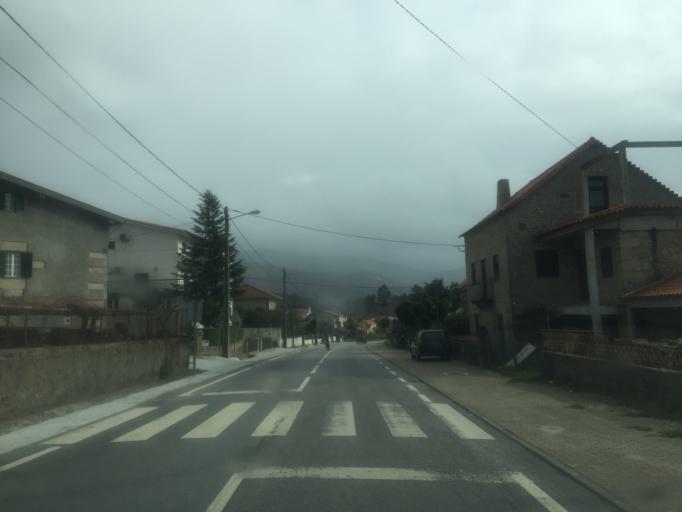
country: PT
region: Guarda
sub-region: Seia
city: Seia
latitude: 40.4012
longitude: -7.7424
